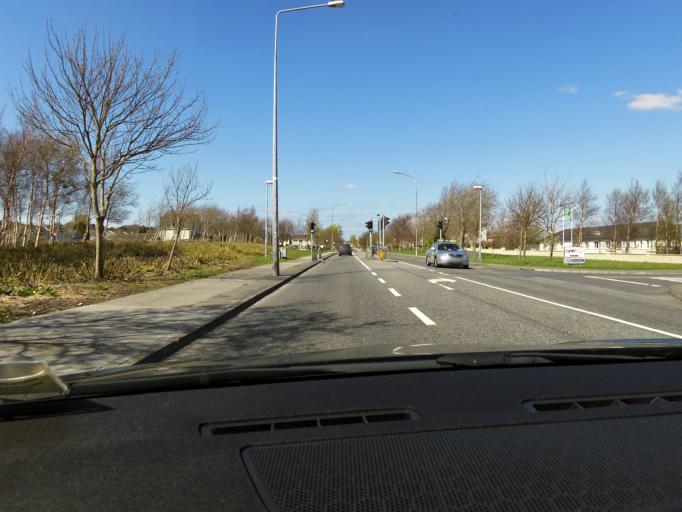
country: IE
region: Connaught
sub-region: County Galway
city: Gaillimh
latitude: 53.2826
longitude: -9.0722
